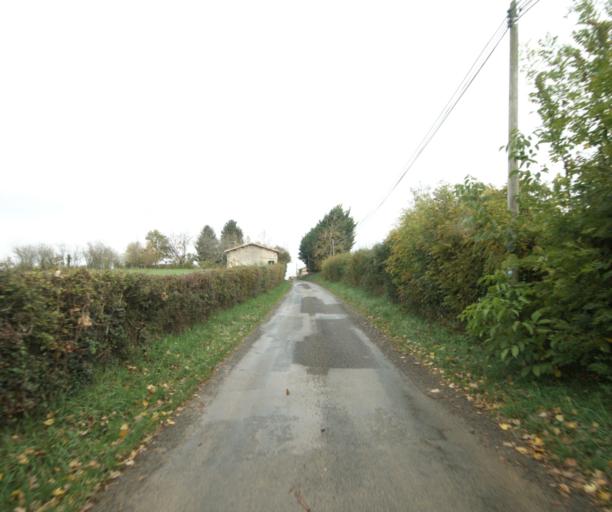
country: FR
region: Rhone-Alpes
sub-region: Departement de l'Ain
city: Pont-de-Vaux
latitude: 46.4721
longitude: 4.8924
